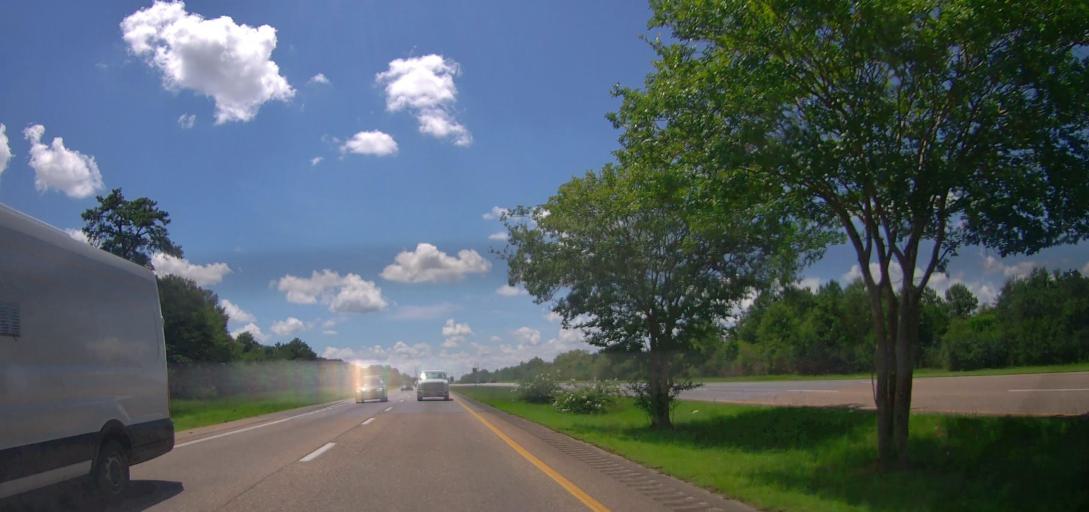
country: US
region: Alabama
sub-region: Montgomery County
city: Montgomery
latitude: 32.4225
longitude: -86.2646
